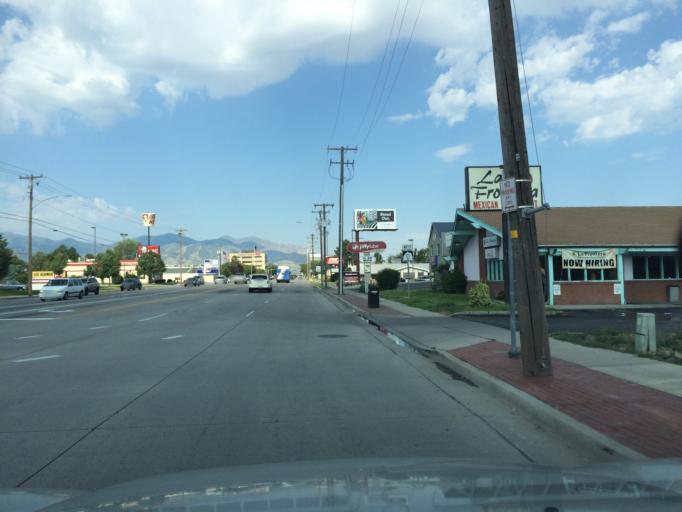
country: US
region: Utah
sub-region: Salt Lake County
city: West Valley City
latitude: 40.6967
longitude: -111.9811
